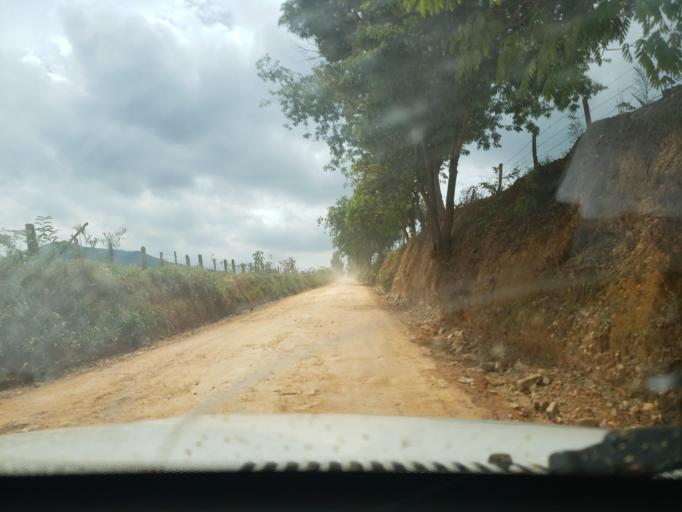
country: BR
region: Minas Gerais
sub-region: Boa Esperanca
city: Boa Esperanca
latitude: -20.9941
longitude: -45.5942
